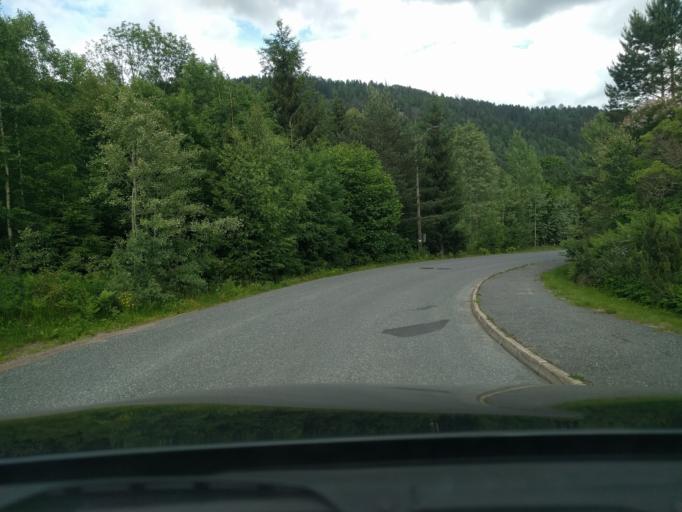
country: NO
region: Telemark
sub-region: Siljan
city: Siljan
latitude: 59.2905
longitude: 9.7151
